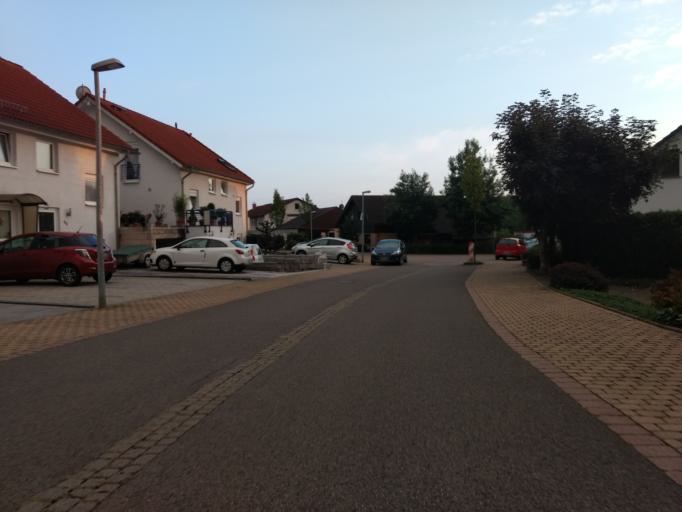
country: DE
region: Saarland
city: Dillingen
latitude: 49.3683
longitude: 6.7158
